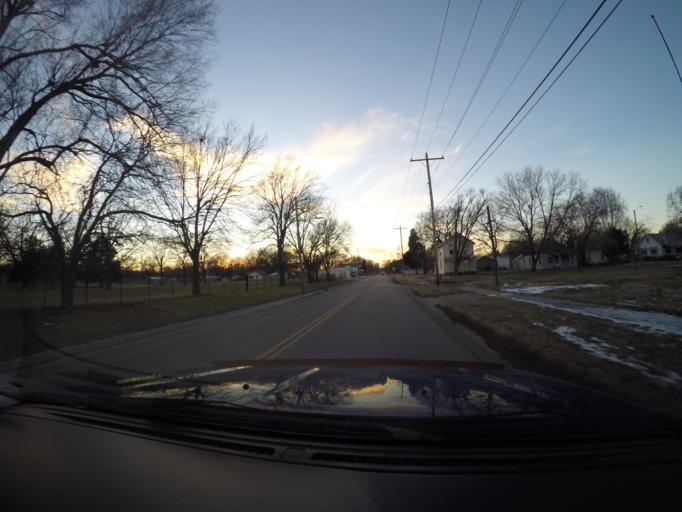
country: US
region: Kansas
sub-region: Shawnee County
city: Topeka
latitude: 39.0443
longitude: -95.6545
